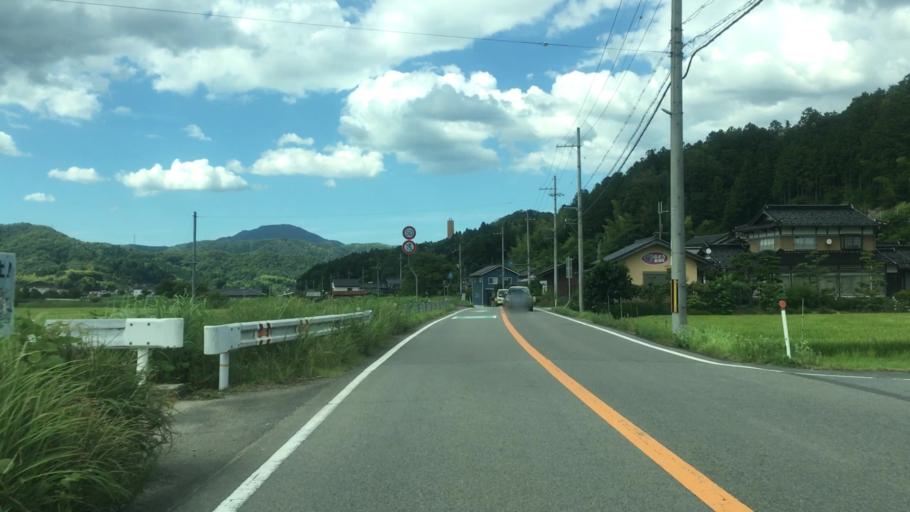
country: JP
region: Hyogo
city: Toyooka
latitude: 35.5391
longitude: 134.7900
